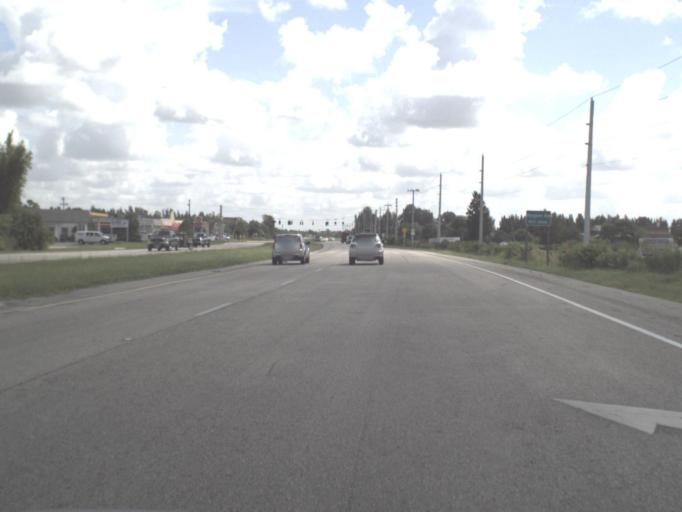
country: US
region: Florida
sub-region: Charlotte County
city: Punta Gorda
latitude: 26.9422
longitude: -82.0133
